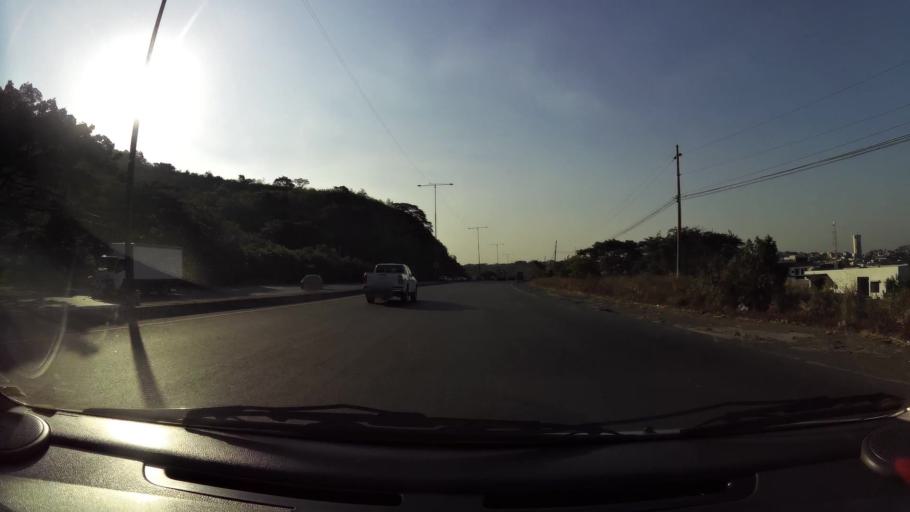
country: EC
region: Guayas
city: Santa Lucia
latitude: -2.1658
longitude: -79.9479
